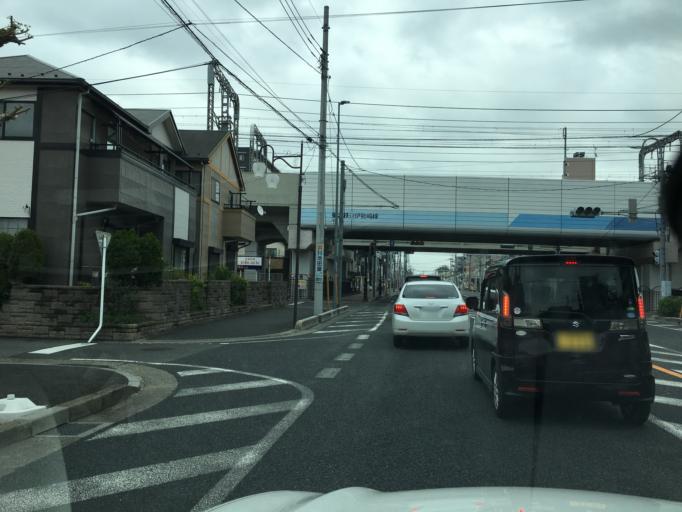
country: JP
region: Saitama
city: Koshigaya
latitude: 35.8650
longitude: 139.7914
